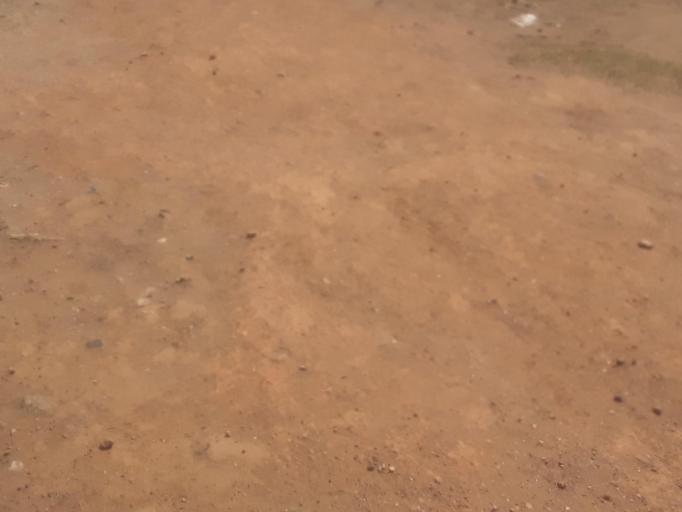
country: ZM
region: Lusaka
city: Lusaka
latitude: -15.3526
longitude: 28.2907
